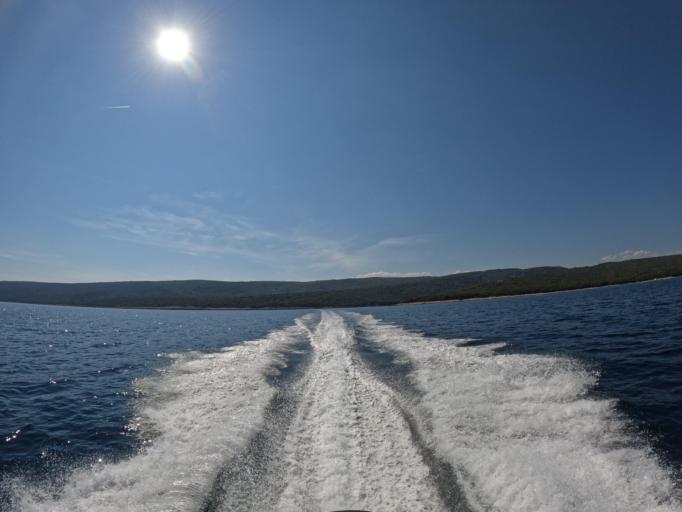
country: HR
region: Primorsko-Goranska
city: Cres
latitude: 44.9460
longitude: 14.4780
